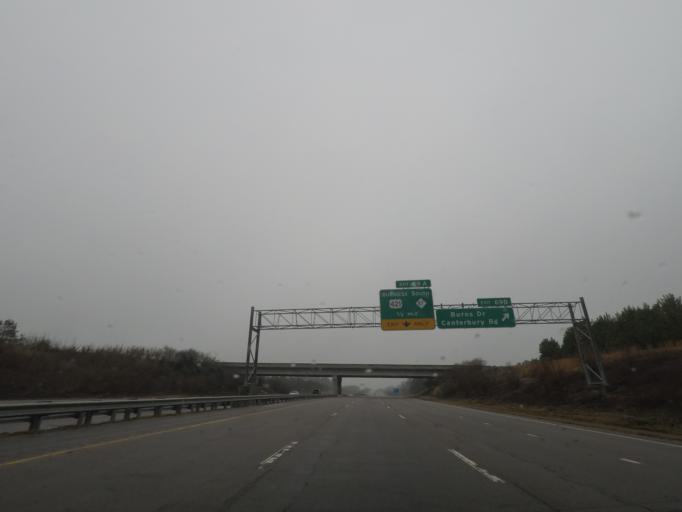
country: US
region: North Carolina
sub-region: Lee County
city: Sanford
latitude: 35.5039
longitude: -79.1907
